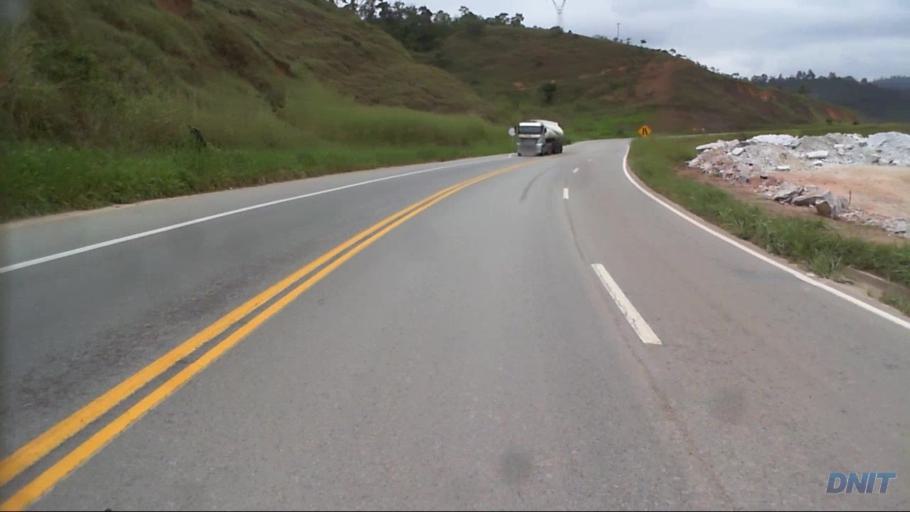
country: BR
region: Minas Gerais
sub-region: Nova Era
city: Nova Era
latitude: -19.6398
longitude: -42.8993
